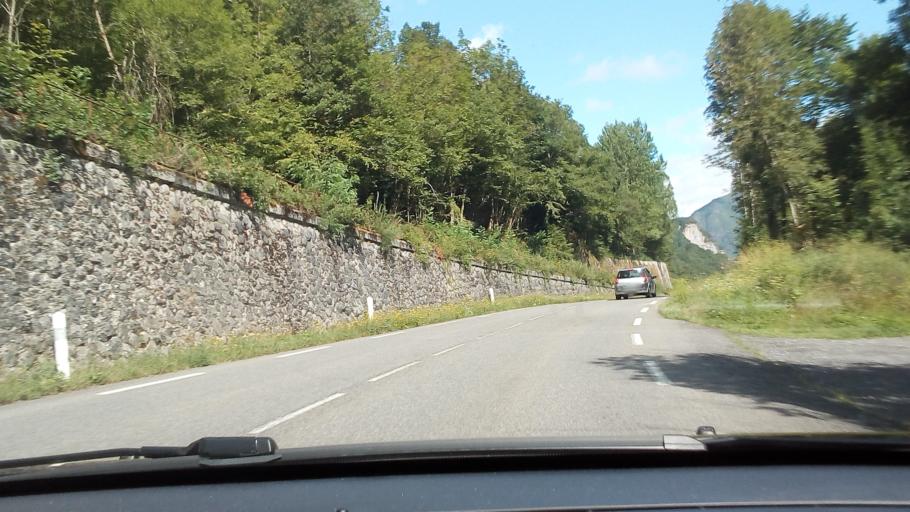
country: FR
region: Aquitaine
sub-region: Departement des Pyrenees-Atlantiques
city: Laruns
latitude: 42.8956
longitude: -0.5661
